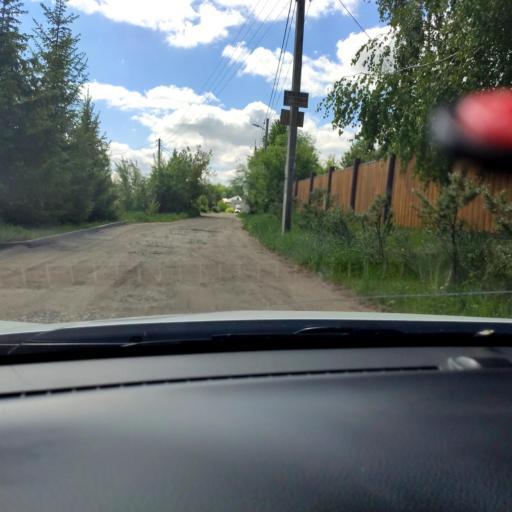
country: RU
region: Tatarstan
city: Stolbishchi
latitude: 55.7529
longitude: 49.2563
